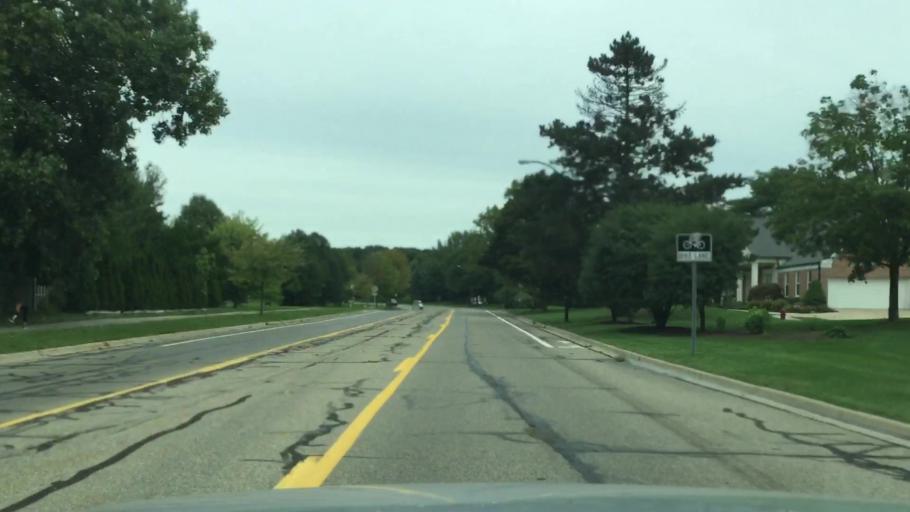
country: US
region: Michigan
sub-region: Washtenaw County
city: Ann Arbor
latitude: 42.3132
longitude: -83.6927
